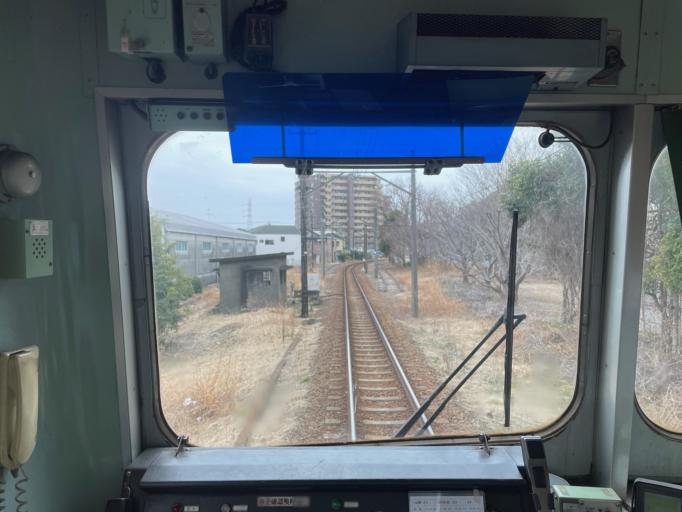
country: JP
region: Shizuoka
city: Fuji
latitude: 35.1628
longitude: 138.7002
